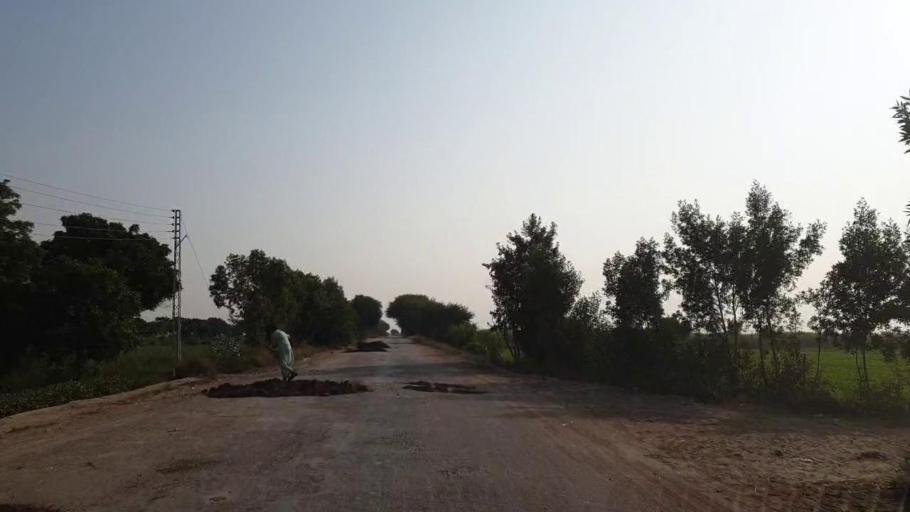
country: PK
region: Sindh
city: Bulri
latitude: 24.9853
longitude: 68.3919
